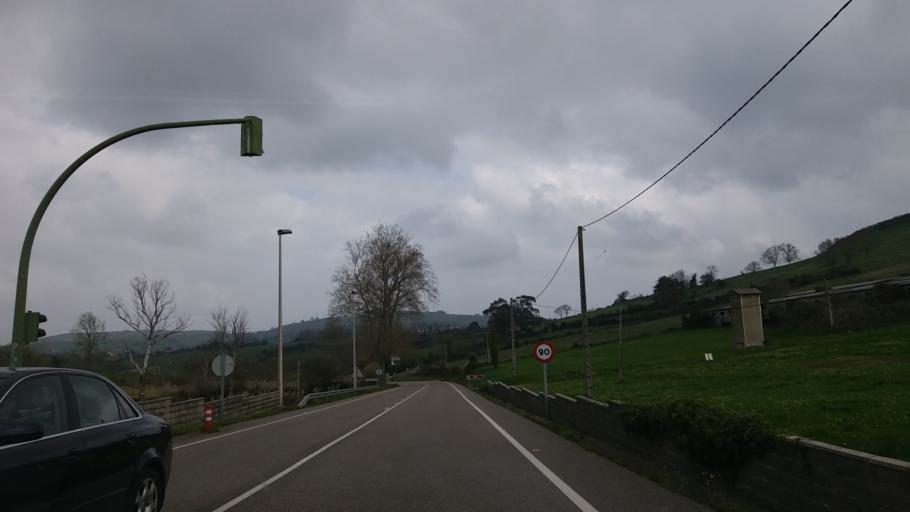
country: ES
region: Cantabria
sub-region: Provincia de Cantabria
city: Santillana
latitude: 43.3757
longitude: -4.0974
